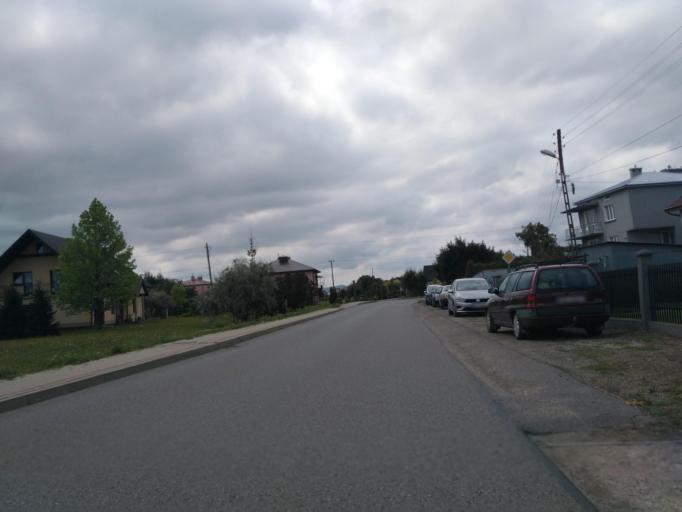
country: PL
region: Subcarpathian Voivodeship
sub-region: Powiat krosnienski
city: Kroscienko Wyzne
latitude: 49.6446
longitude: 21.8227
